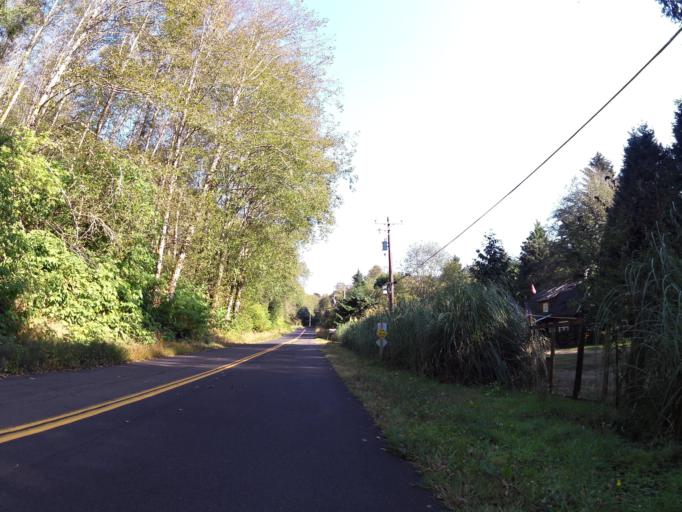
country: US
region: Oregon
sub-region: Lincoln County
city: Rose Lodge
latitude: 45.0790
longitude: -123.9403
